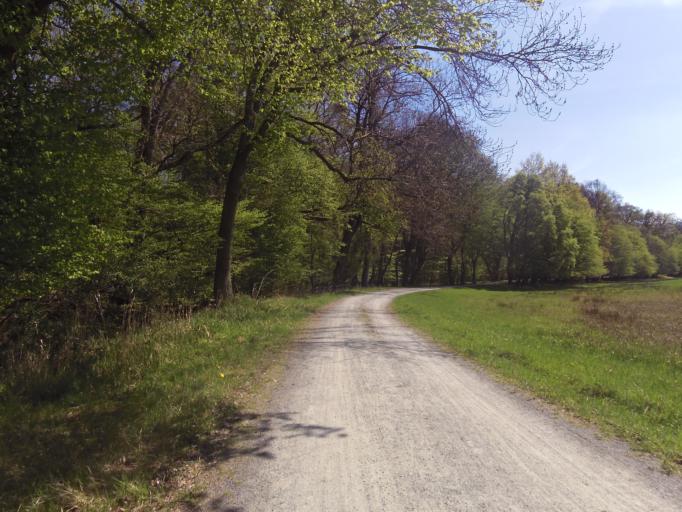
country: DE
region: Hesse
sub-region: Regierungsbezirk Darmstadt
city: Nauheim
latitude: 49.9790
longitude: 8.5194
